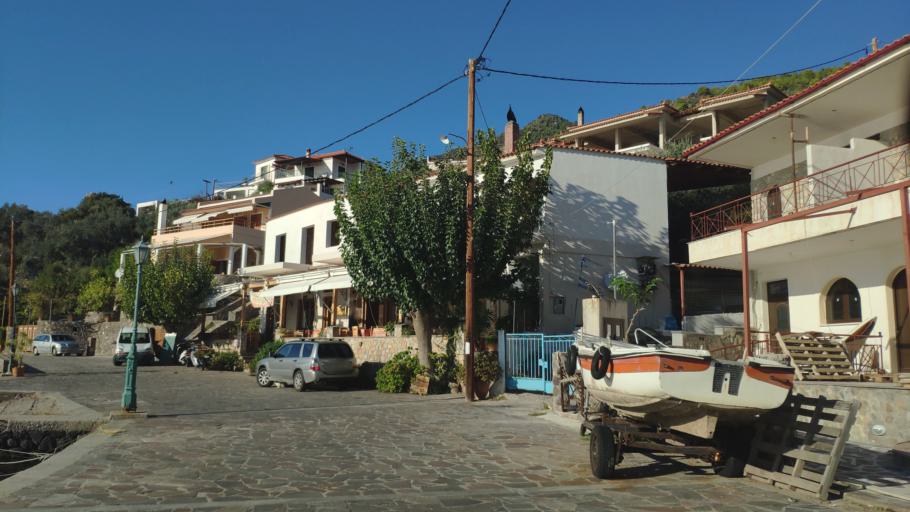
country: GR
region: Attica
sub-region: Nomos Piraios
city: Megalochori
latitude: 37.5938
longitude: 23.3397
